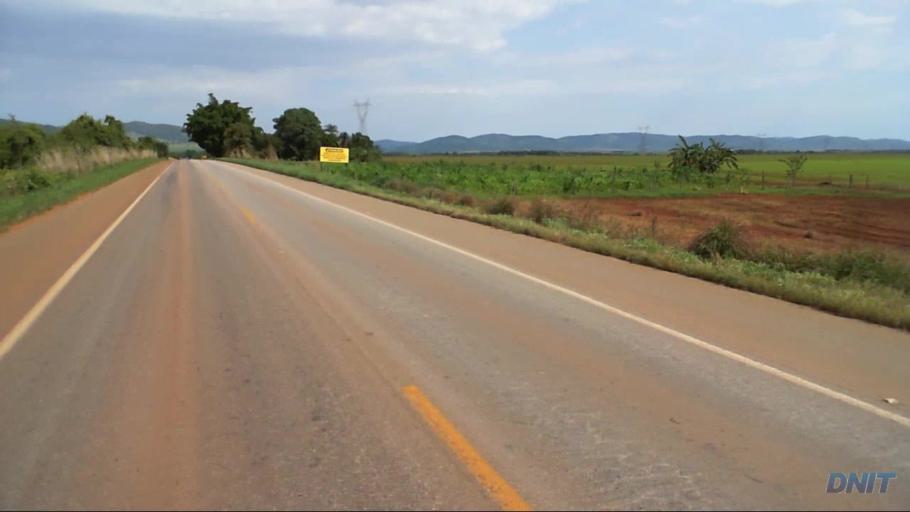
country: BR
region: Goias
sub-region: Barro Alto
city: Barro Alto
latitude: -15.0694
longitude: -48.8708
